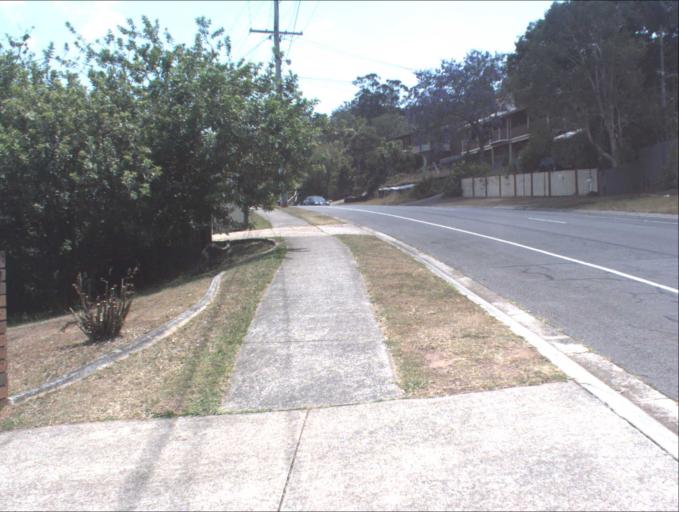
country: AU
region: Queensland
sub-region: Logan
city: Slacks Creek
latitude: -27.6634
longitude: 153.1923
